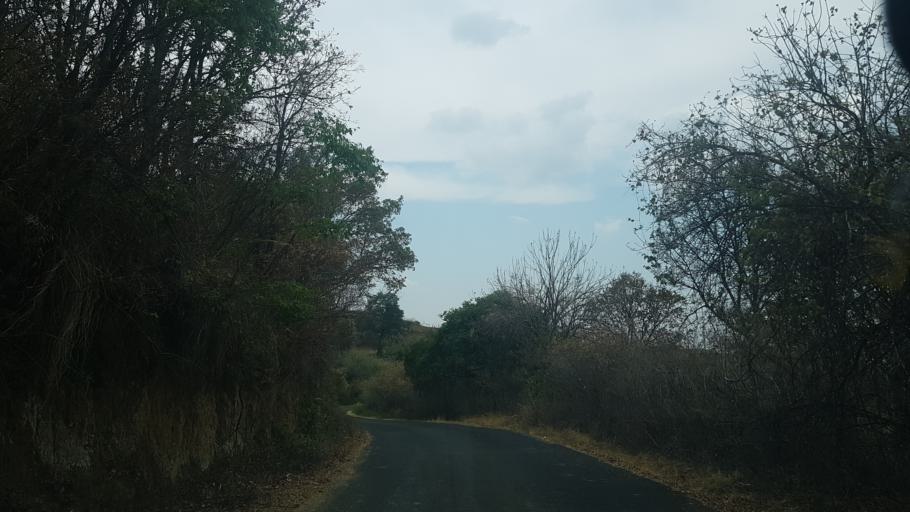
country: MX
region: Puebla
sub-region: Atzitzihuacan
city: Santiago Atzitzihuacan
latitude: 18.8395
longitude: -98.6154
